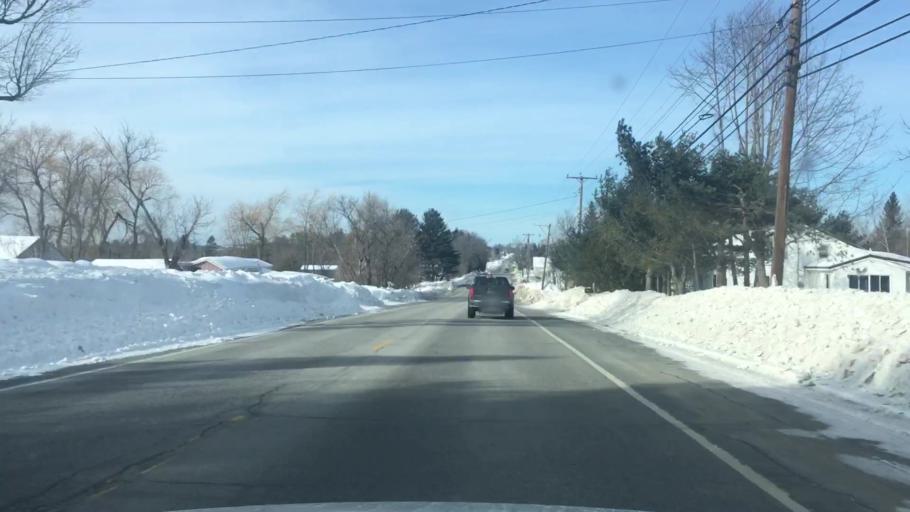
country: US
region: Maine
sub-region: Penobscot County
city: Charleston
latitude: 45.0108
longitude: -69.0262
